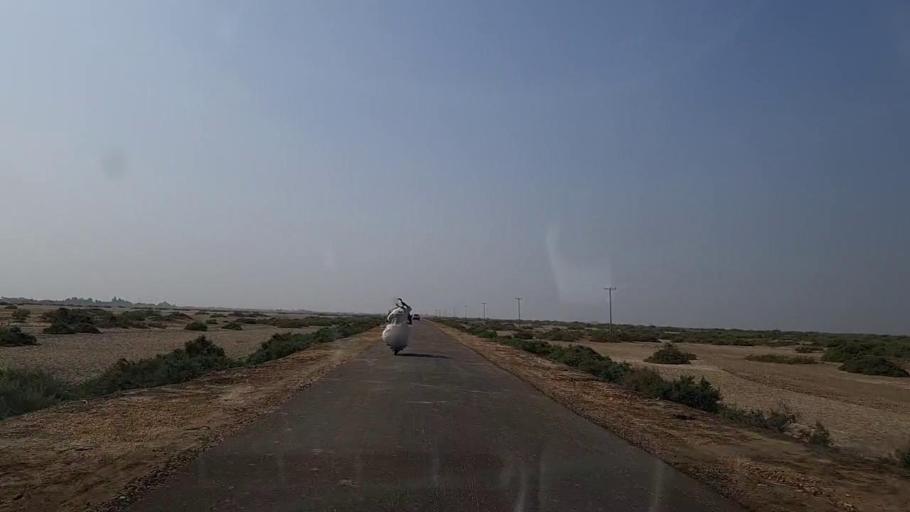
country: PK
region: Sindh
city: Mirpur Sakro
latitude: 24.5289
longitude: 67.5848
